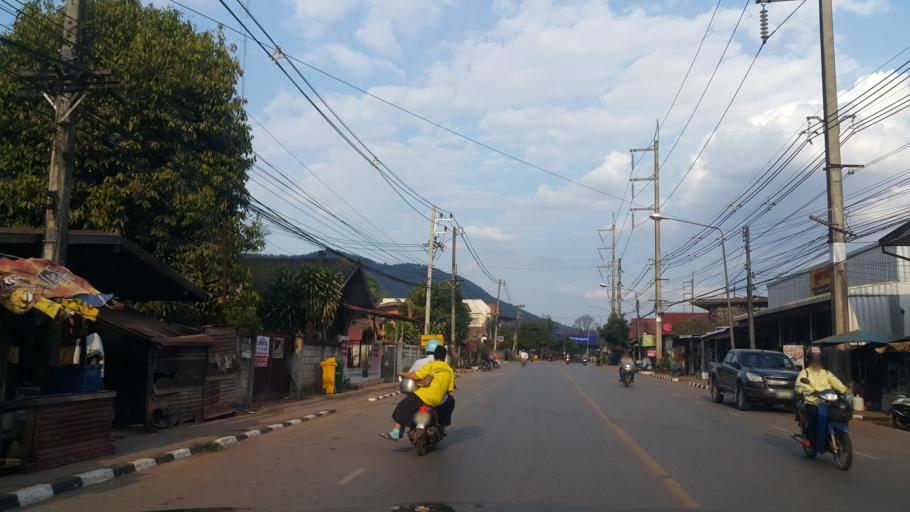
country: TH
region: Loei
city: Dan Sai
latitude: 17.2730
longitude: 101.1507
